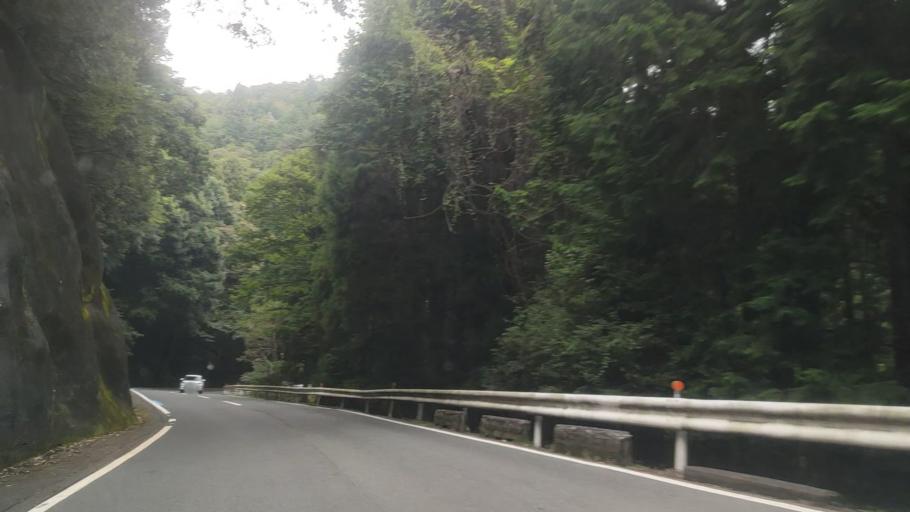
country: JP
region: Wakayama
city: Koya
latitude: 34.2103
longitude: 135.5465
